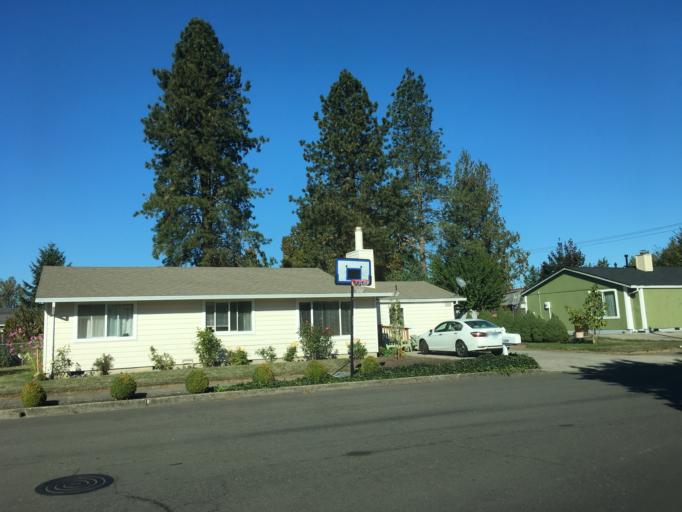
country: US
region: Oregon
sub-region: Multnomah County
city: Gresham
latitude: 45.4940
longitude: -122.3998
